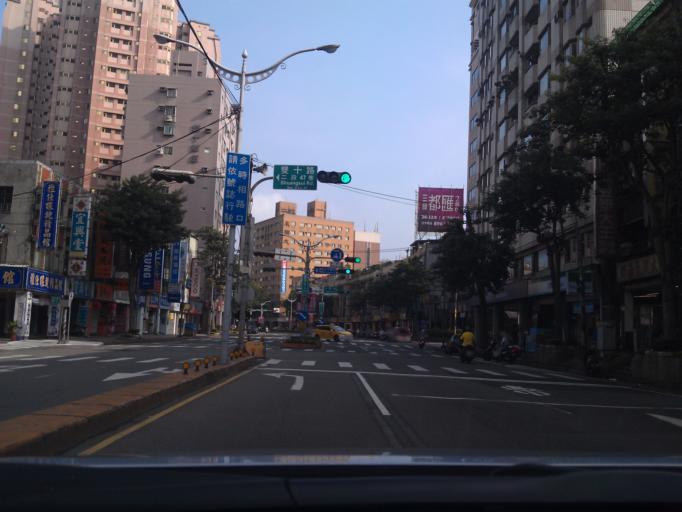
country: TW
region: Taipei
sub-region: Taipei
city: Banqiao
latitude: 25.0261
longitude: 121.4768
